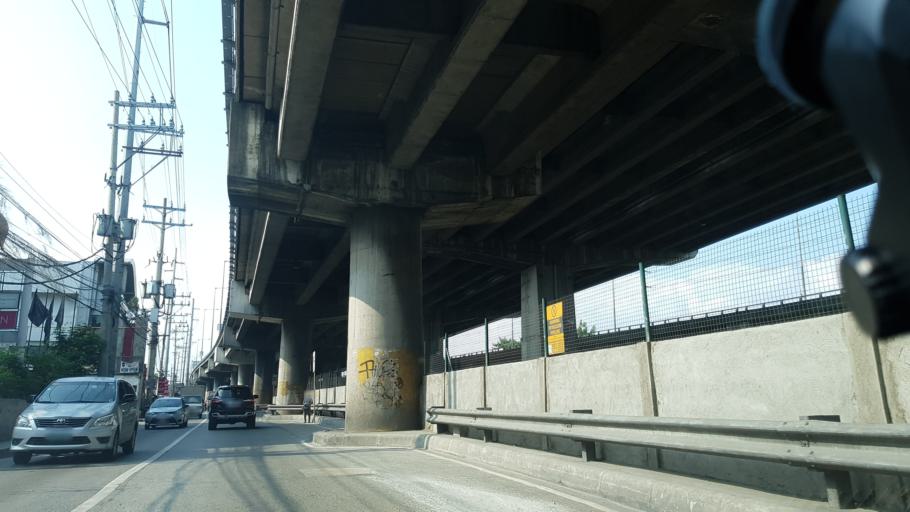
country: PH
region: Calabarzon
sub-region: Province of Rizal
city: Taguig
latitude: 14.4891
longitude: 121.0440
